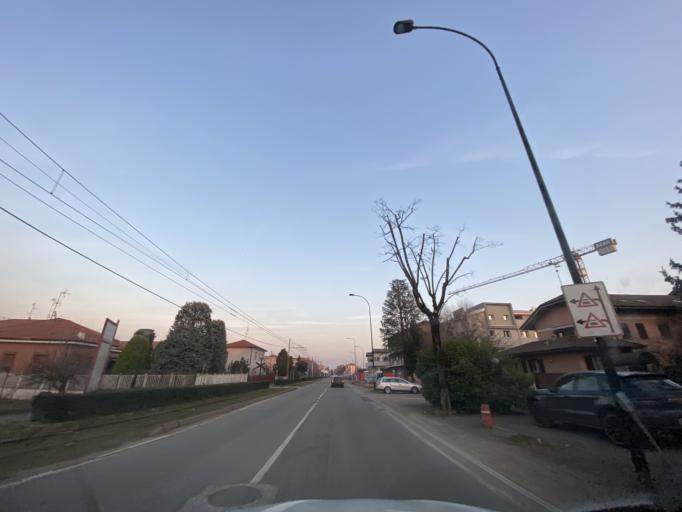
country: IT
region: Lombardy
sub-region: Provincia di Monza e Brianza
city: Limbiate
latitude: 45.6003
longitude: 9.1301
